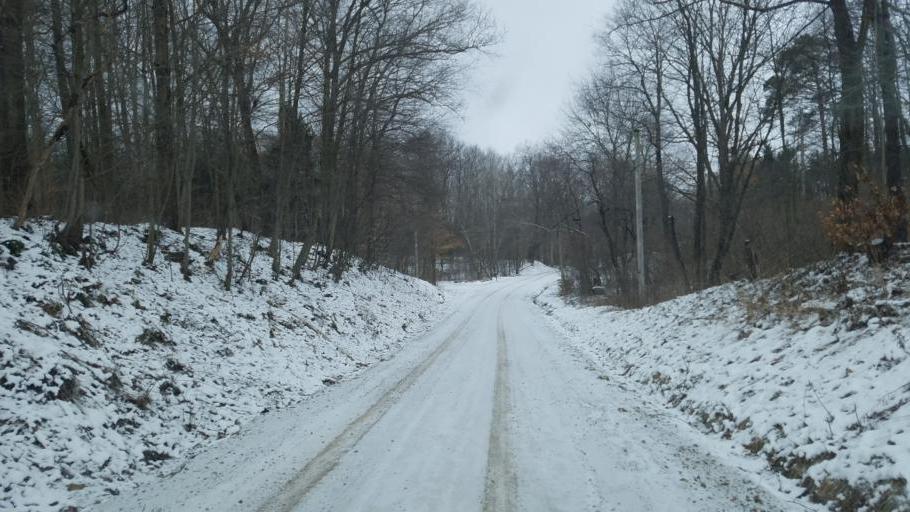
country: US
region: Pennsylvania
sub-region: Crawford County
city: Cochranton
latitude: 41.4637
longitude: -79.9795
